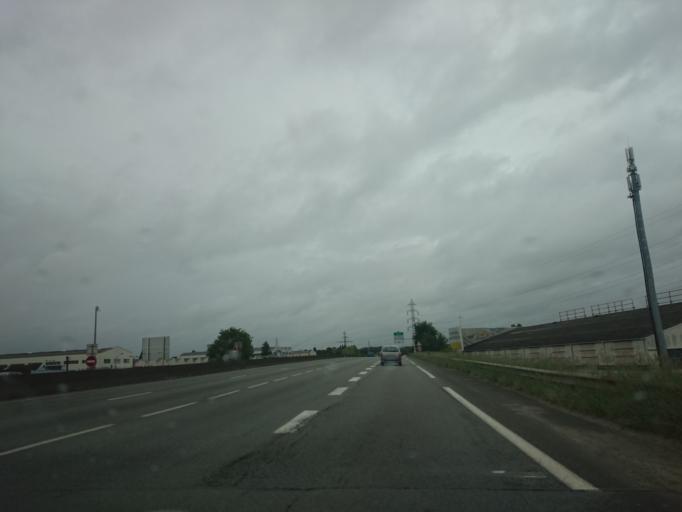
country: FR
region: Brittany
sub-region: Departement d'Ille-et-Vilaine
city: Vezin-le-Coquet
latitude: 48.1059
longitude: -1.7169
